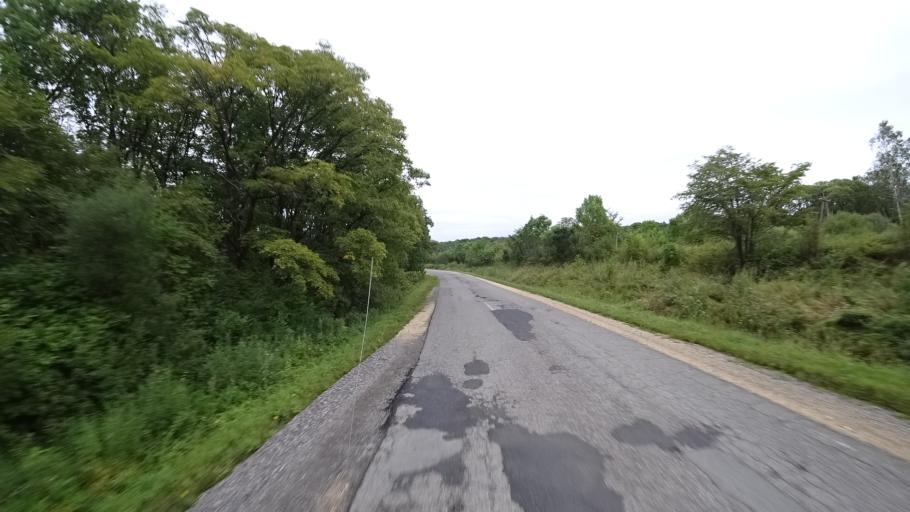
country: RU
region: Primorskiy
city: Rettikhovka
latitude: 44.1643
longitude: 132.7630
